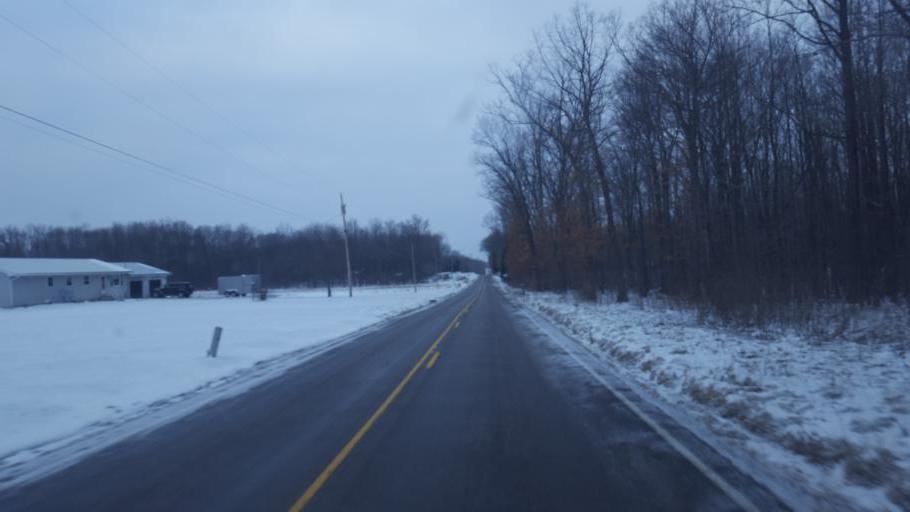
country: US
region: Pennsylvania
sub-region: Mercer County
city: Stoneboro
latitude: 41.4055
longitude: -80.0208
